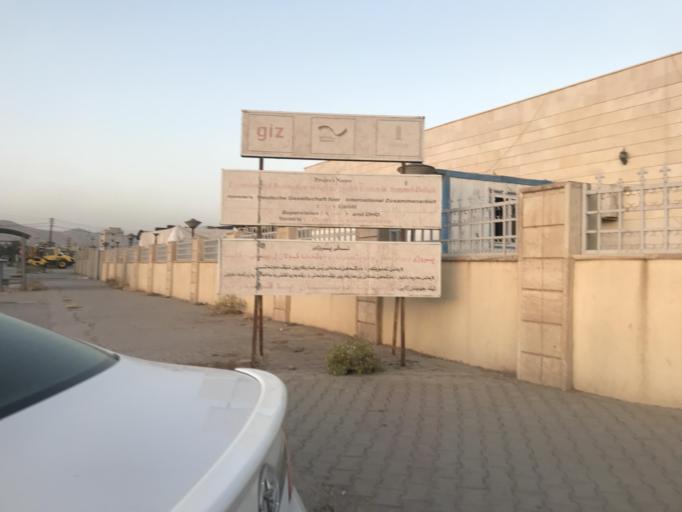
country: IQ
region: Dahuk
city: Saymayl
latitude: 36.8610
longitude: 42.8368
